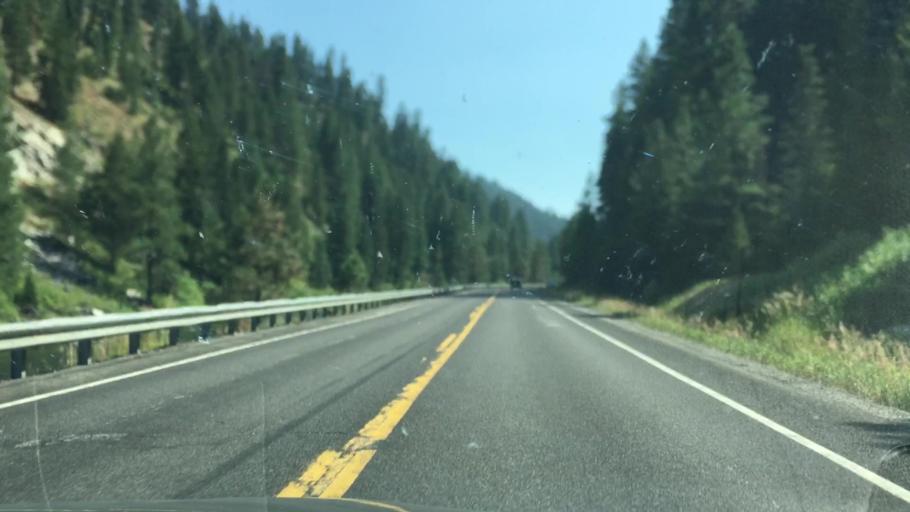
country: US
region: Idaho
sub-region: Valley County
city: Cascade
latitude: 44.2409
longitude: -116.1030
